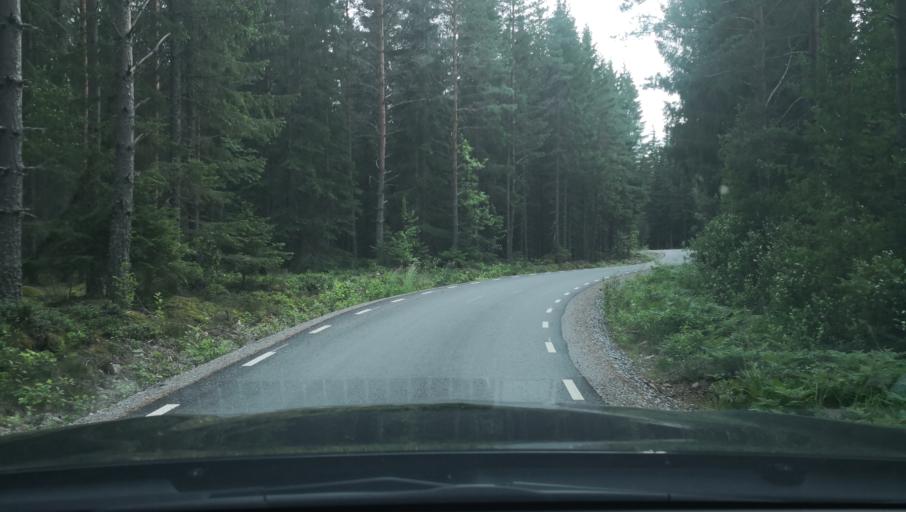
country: SE
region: Vaestmanland
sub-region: Surahammars Kommun
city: Surahammar
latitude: 59.6660
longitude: 16.1372
